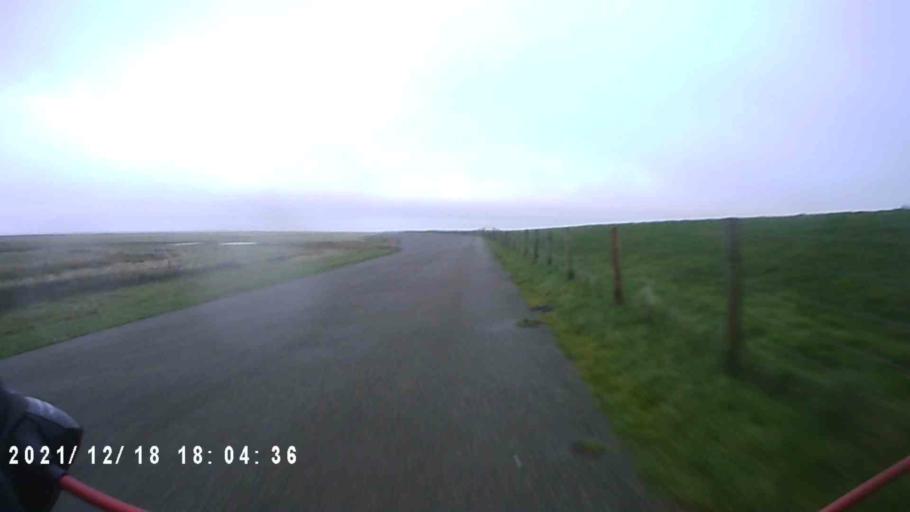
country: NL
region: Friesland
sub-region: Gemeente Dongeradeel
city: Holwerd
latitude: 53.3825
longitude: 5.9029
